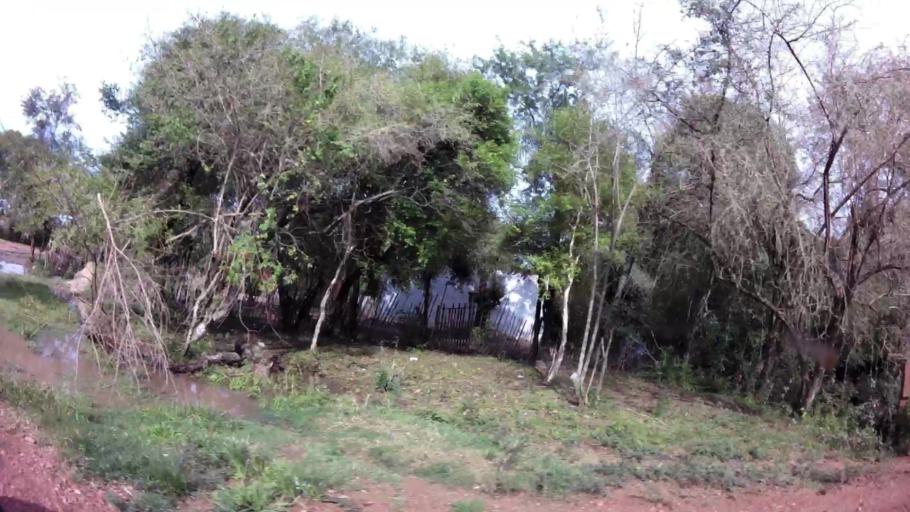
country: PY
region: Central
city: Limpio
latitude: -25.1728
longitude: -57.4943
